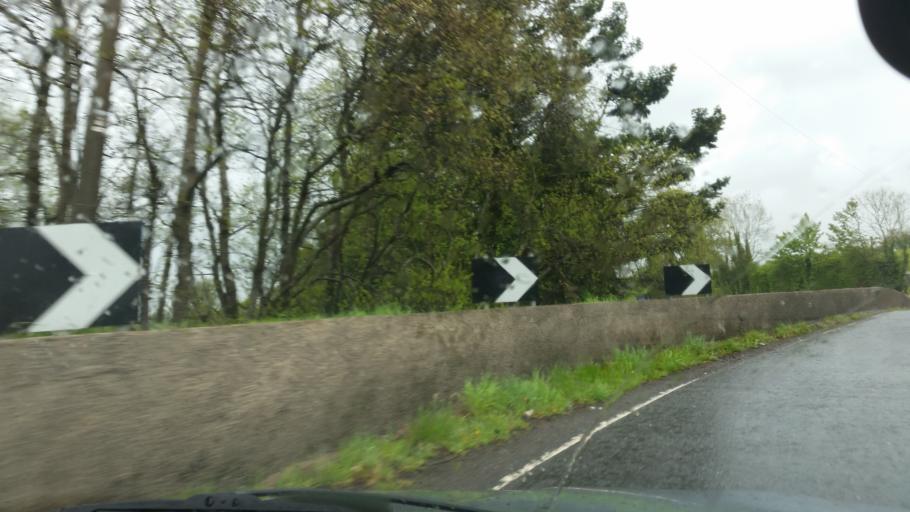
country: GB
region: Northern Ireland
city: Fintona
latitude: 54.5288
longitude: -7.2950
